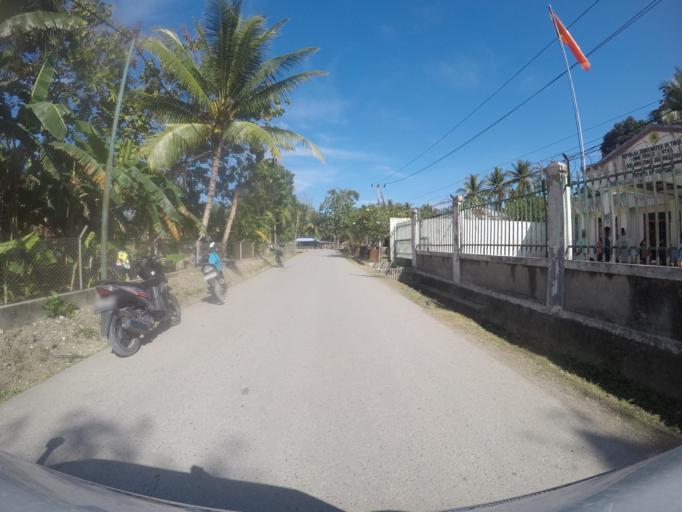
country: TL
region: Viqueque
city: Viqueque
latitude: -8.8552
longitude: 126.3628
